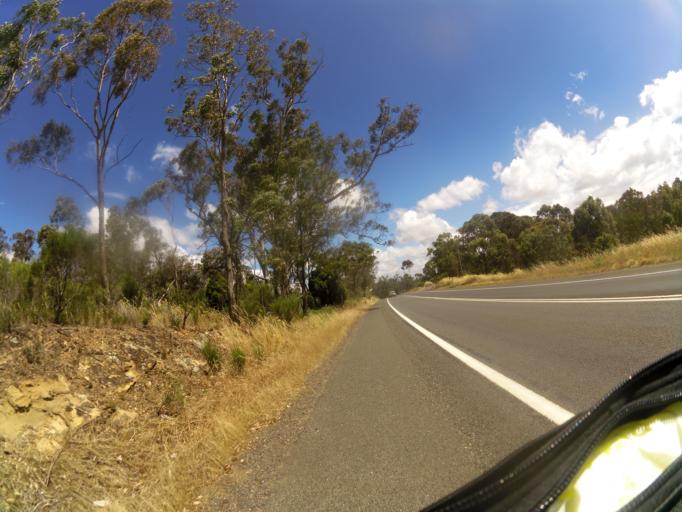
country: AU
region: Victoria
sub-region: Mount Alexander
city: Castlemaine
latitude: -37.0203
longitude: 144.2390
